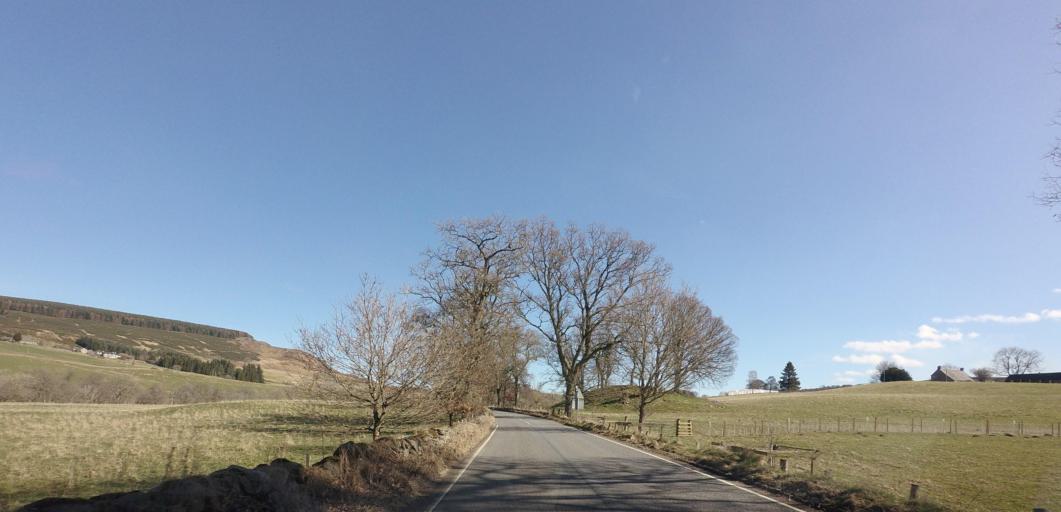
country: GB
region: Scotland
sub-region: Perth and Kinross
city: Methven
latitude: 56.5435
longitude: -3.6532
